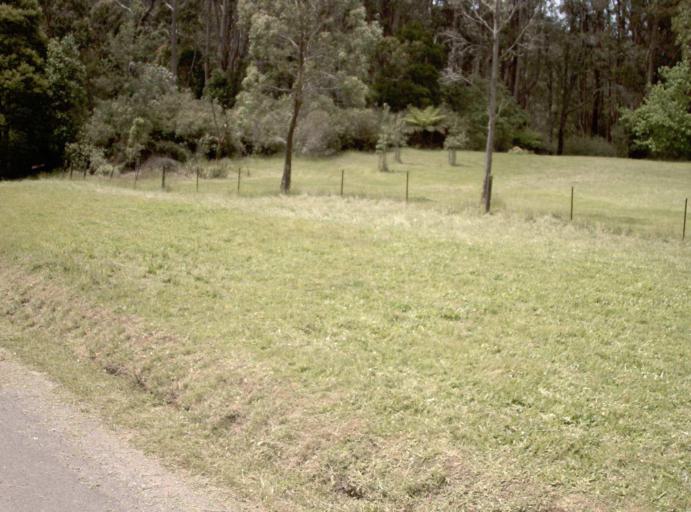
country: AU
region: Victoria
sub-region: Latrobe
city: Traralgon
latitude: -38.4273
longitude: 146.5659
